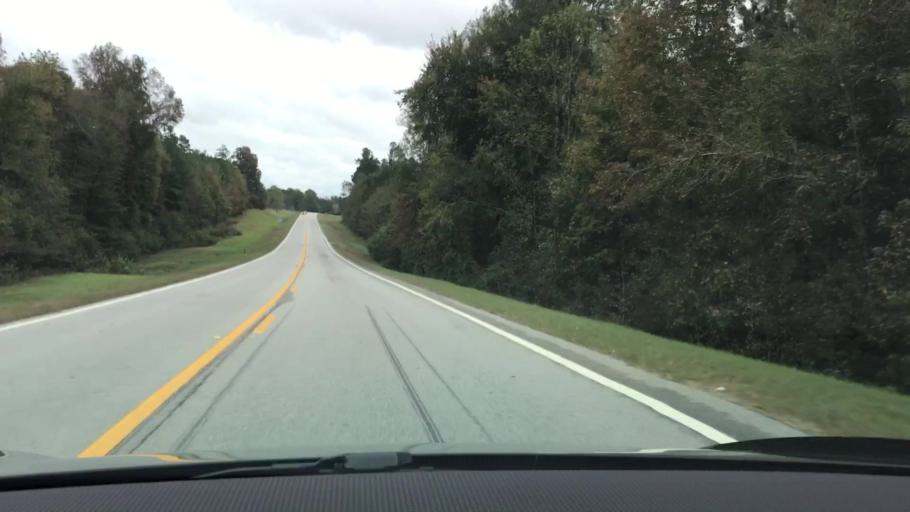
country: US
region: Georgia
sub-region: Glascock County
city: Gibson
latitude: 33.2648
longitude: -82.4889
